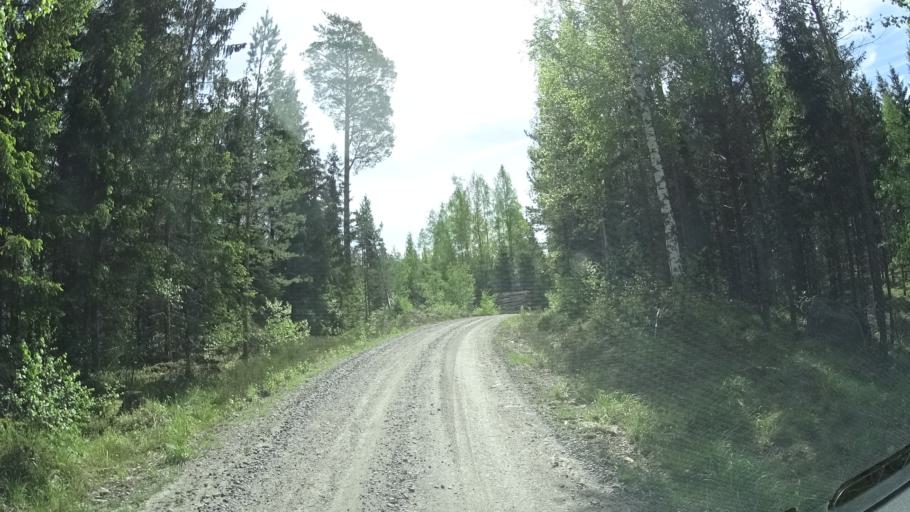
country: SE
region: OEstergoetland
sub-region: Finspangs Kommun
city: Finspang
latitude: 58.7834
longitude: 15.8460
